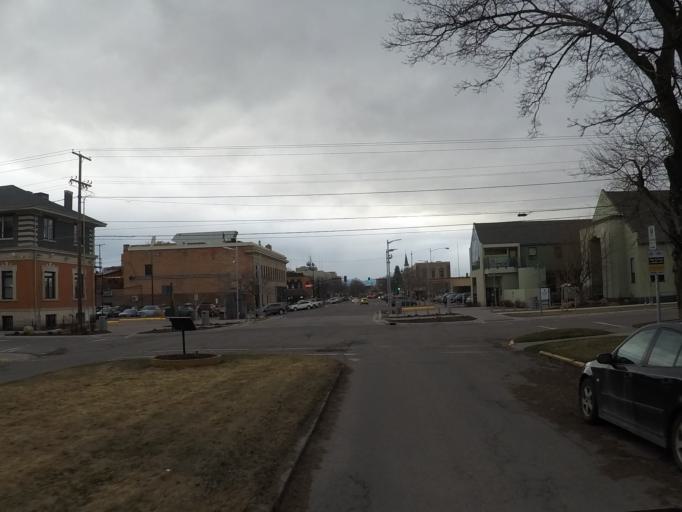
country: US
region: Montana
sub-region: Missoula County
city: Missoula
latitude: 46.8726
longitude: -113.9916
